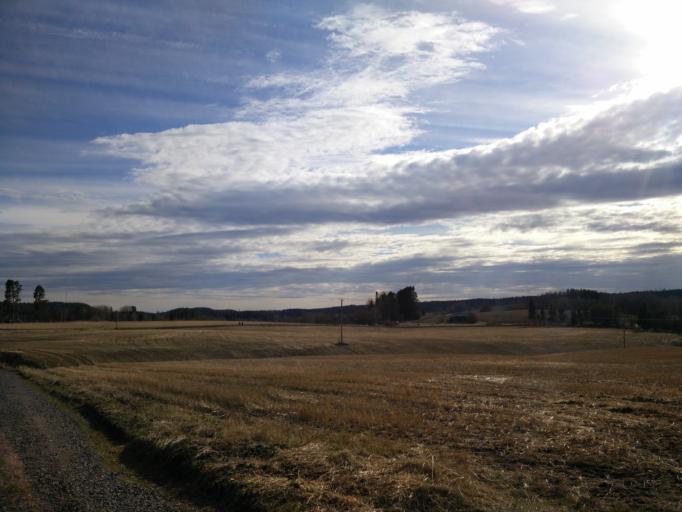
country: FI
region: Pirkanmaa
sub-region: Tampere
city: Orivesi
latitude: 61.7107
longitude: 24.3212
